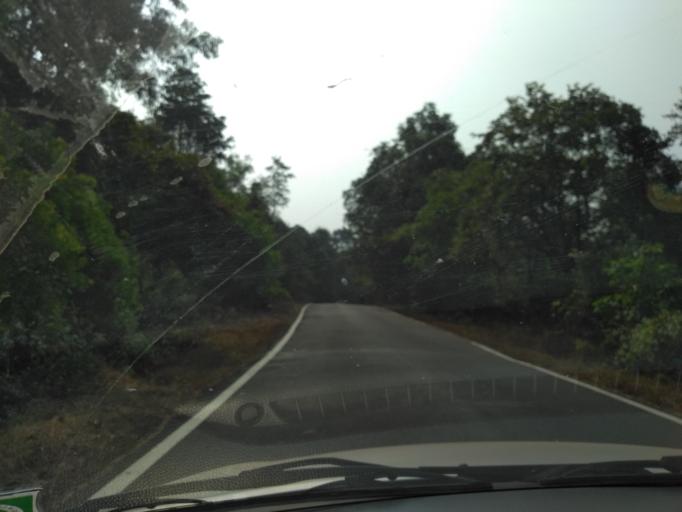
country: IN
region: Goa
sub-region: North Goa
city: Pernem
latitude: 15.7705
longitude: 73.9189
